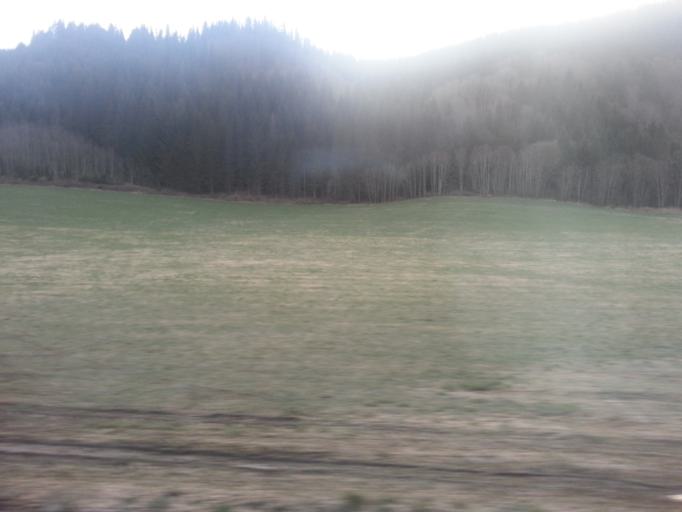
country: NO
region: Sor-Trondelag
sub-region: Melhus
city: Melhus
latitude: 63.2451
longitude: 10.2784
